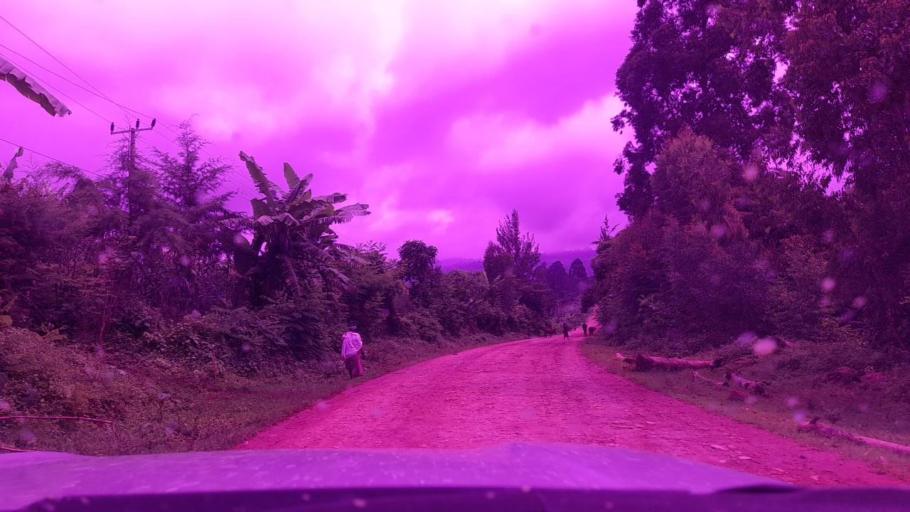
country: ET
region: Southern Nations, Nationalities, and People's Region
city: Bonga
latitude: 7.5454
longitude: 35.8744
